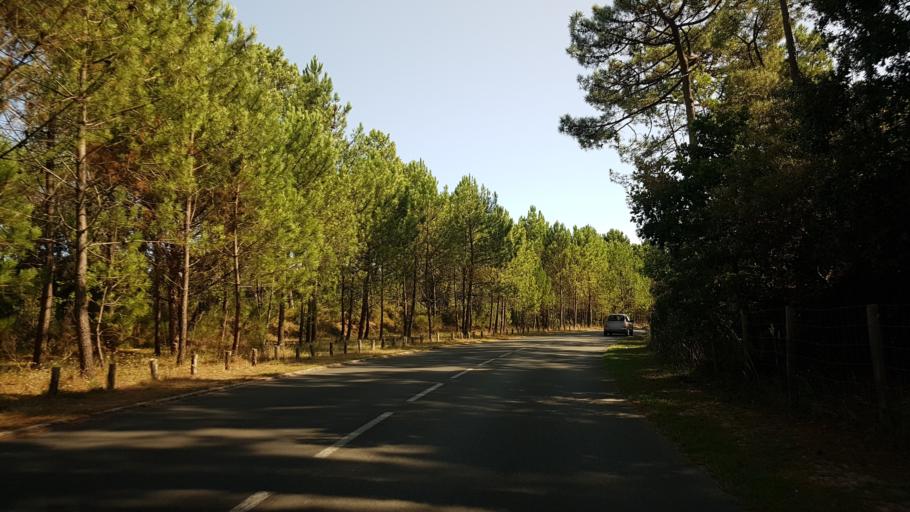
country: FR
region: Poitou-Charentes
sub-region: Departement de la Charente-Maritime
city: Les Mathes
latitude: 45.6980
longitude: -1.1968
